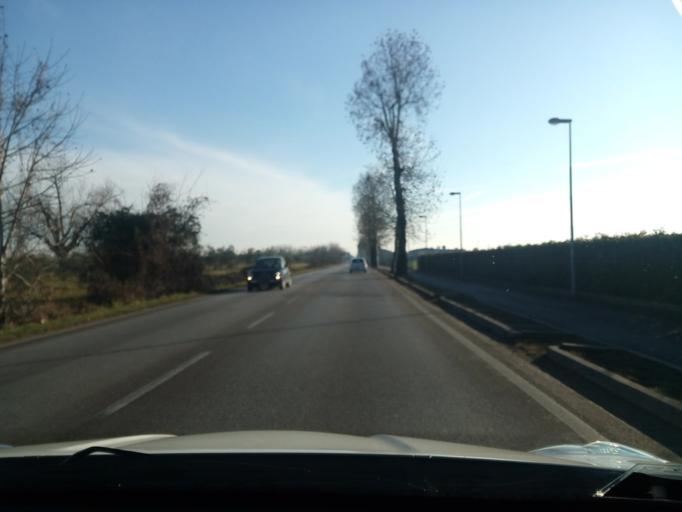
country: IT
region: Veneto
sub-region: Provincia di Vicenza
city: Thiene
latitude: 45.6811
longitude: 11.4855
